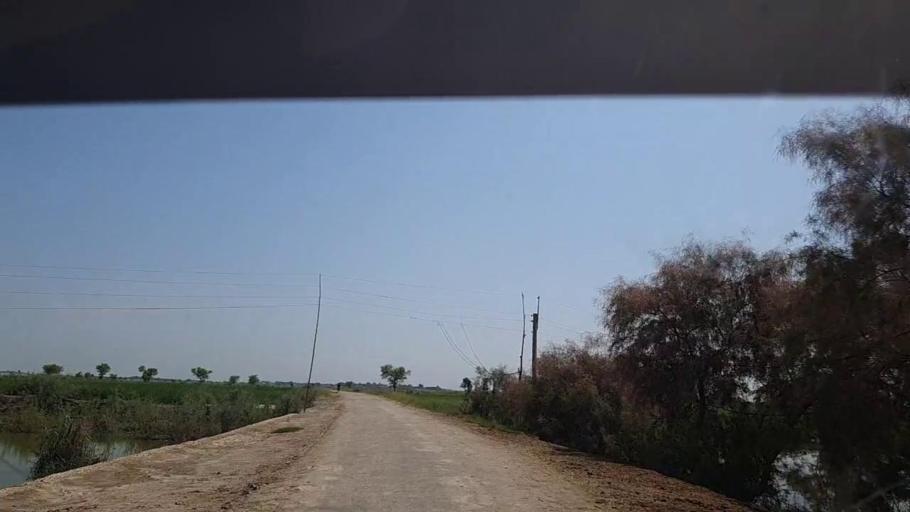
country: PK
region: Sindh
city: Kandhkot
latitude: 28.1816
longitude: 69.1590
